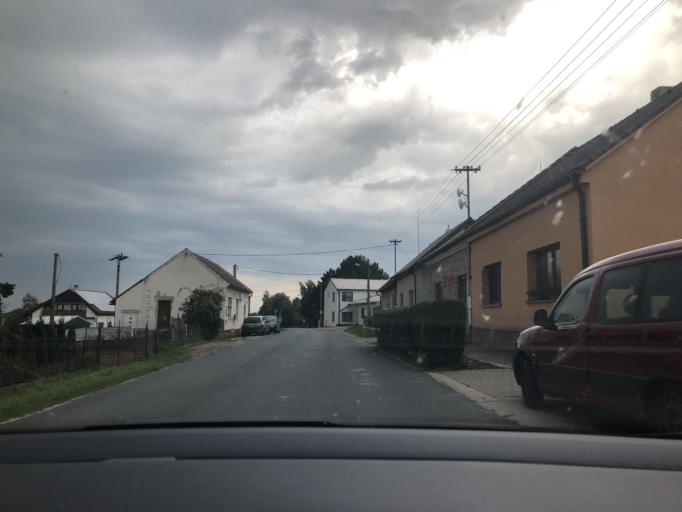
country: CZ
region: Central Bohemia
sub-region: Okres Kolin
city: Tynec nad Labem
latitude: 50.0335
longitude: 15.3608
